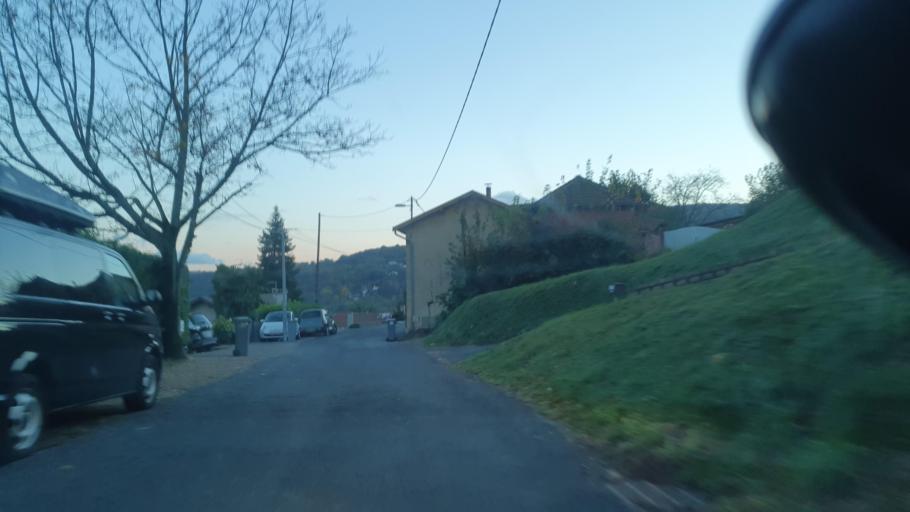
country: FR
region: Rhone-Alpes
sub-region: Departement du Rhone
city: Albigny-sur-Saone
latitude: 45.8475
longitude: 4.8269
